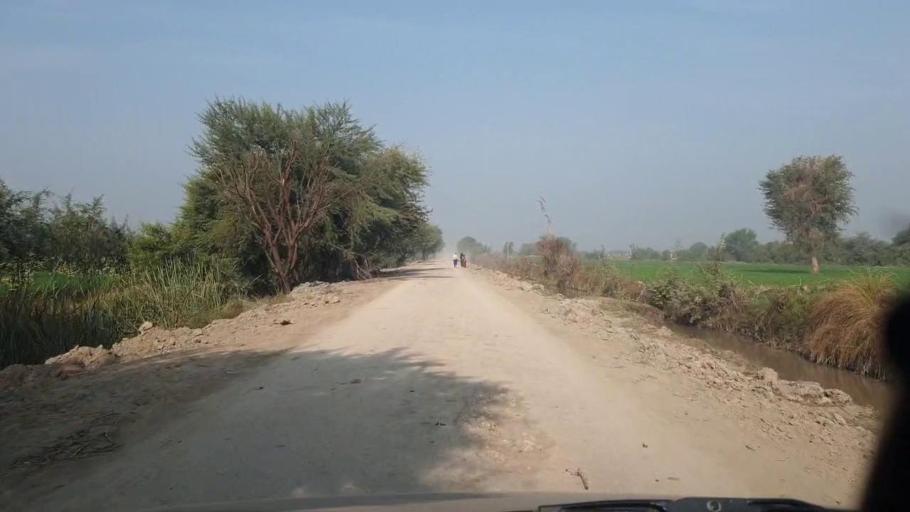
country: PK
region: Sindh
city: Shahdadpur
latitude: 26.0326
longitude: 68.5412
